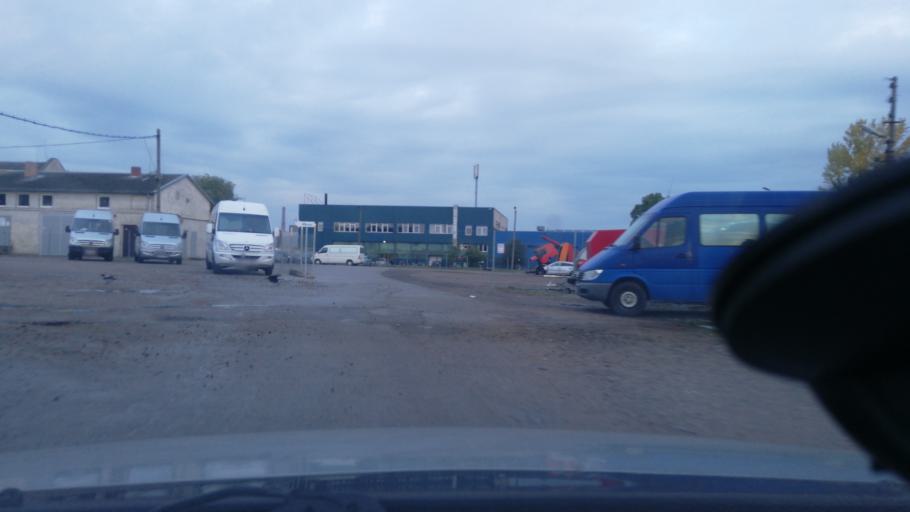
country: LT
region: Klaipedos apskritis
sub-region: Klaipeda
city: Klaipeda
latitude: 55.6875
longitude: 21.1851
